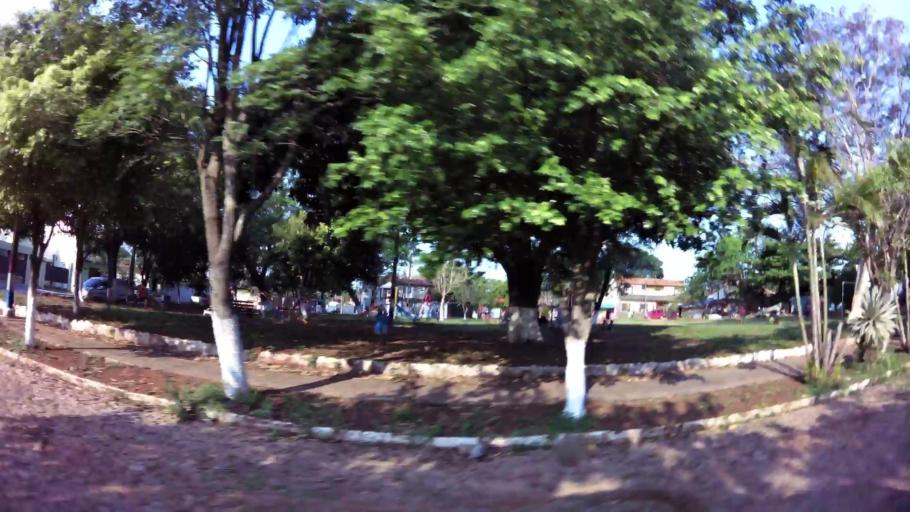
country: PY
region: Central
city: Lambare
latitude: -25.3438
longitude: -57.5961
